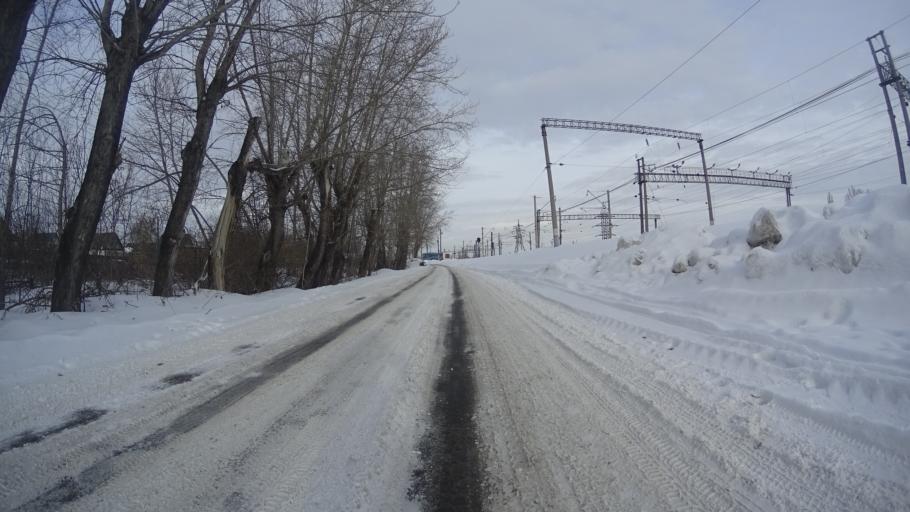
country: RU
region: Chelyabinsk
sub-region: Gorod Chelyabinsk
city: Chelyabinsk
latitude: 55.1268
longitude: 61.4007
